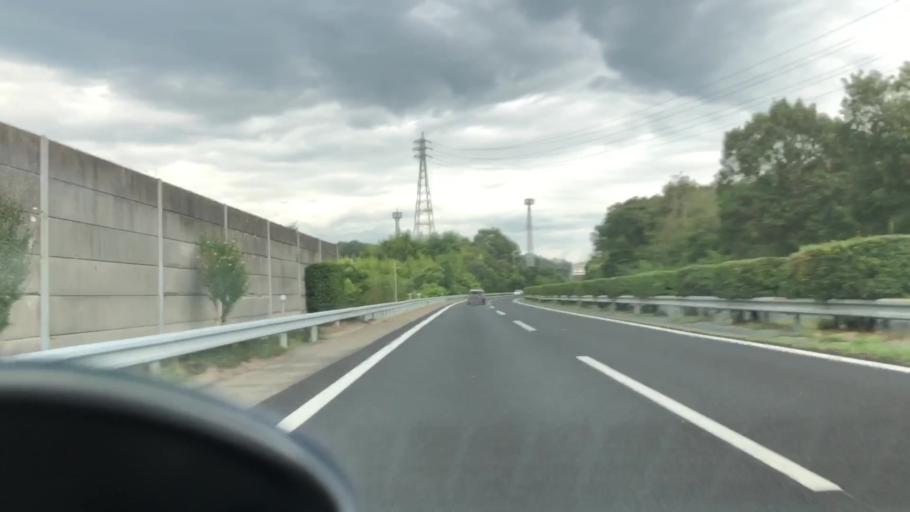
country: JP
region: Hyogo
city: Yashiro
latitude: 34.9371
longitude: 134.8701
